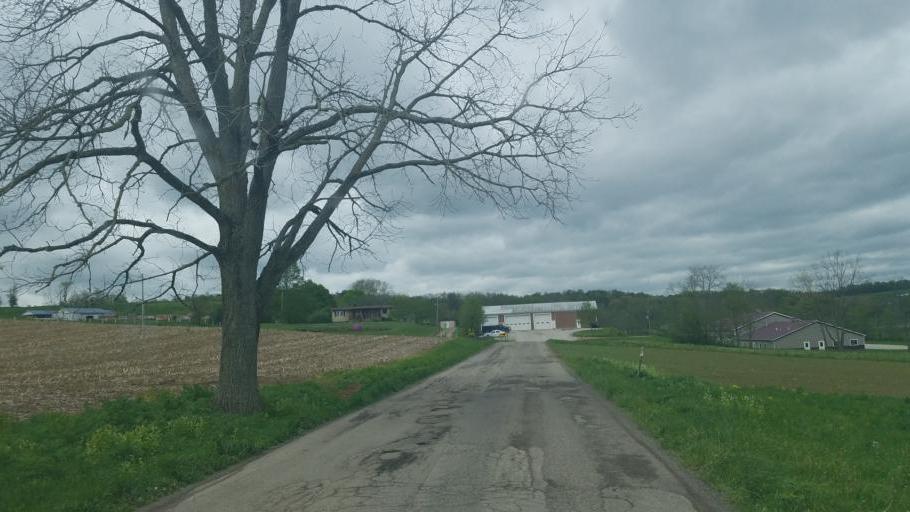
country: US
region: Ohio
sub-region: Knox County
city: Danville
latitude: 40.5387
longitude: -82.3315
